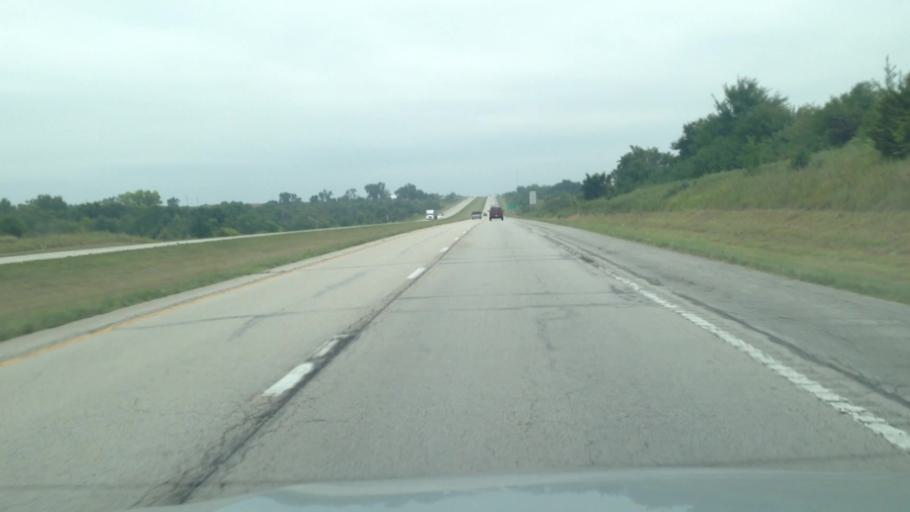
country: US
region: Iowa
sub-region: Decatur County
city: Lamoni
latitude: 40.5385
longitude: -93.9568
